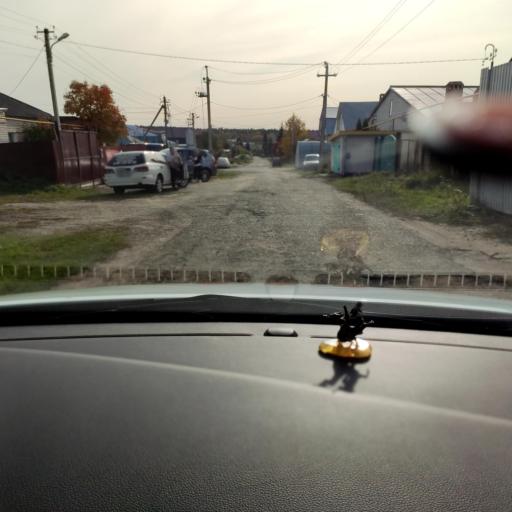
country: RU
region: Tatarstan
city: Vysokaya Gora
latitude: 55.9149
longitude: 49.2947
